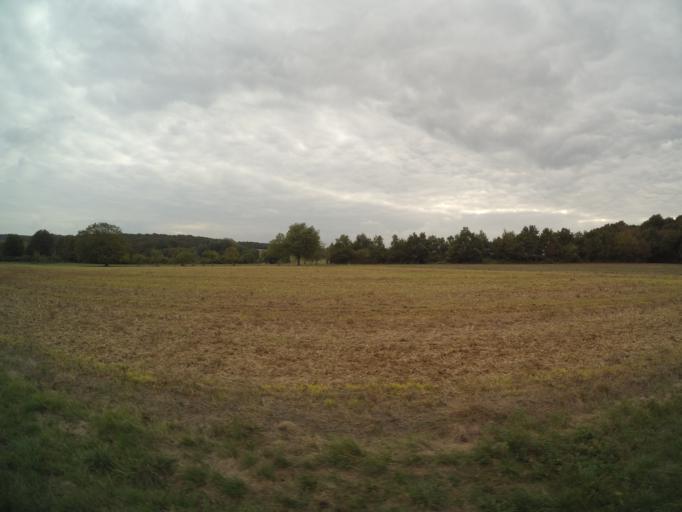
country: FR
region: Centre
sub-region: Departement d'Indre-et-Loire
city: Auzouer-en-Touraine
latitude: 47.5086
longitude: 0.9319
